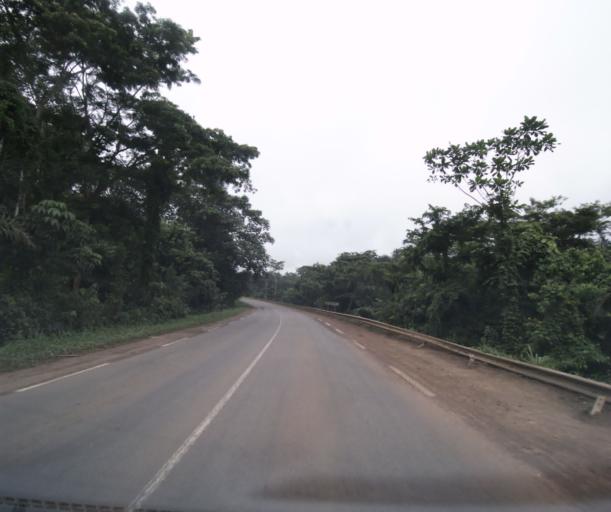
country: CM
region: Centre
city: Mbankomo
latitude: 3.7639
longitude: 11.0983
